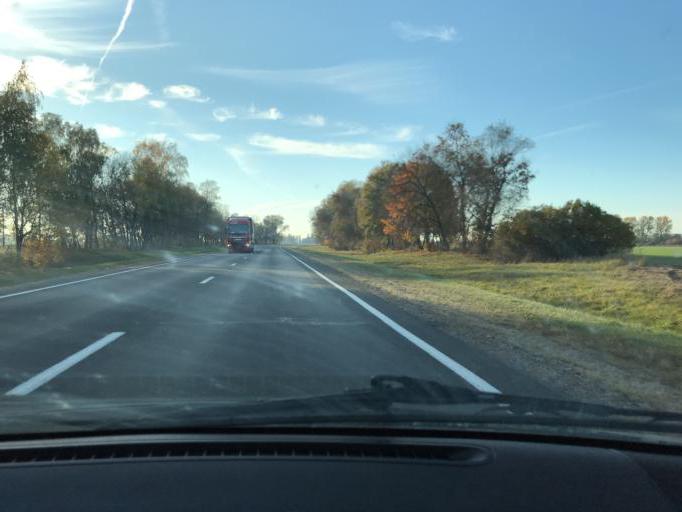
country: BY
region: Brest
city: Horad Kobryn
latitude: 52.2173
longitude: 24.5160
